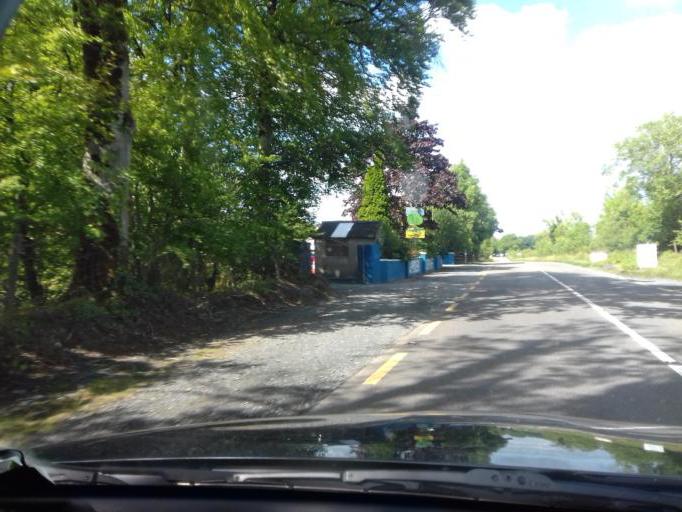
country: IE
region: Leinster
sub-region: Wicklow
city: Blessington
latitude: 53.1447
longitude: -6.5585
